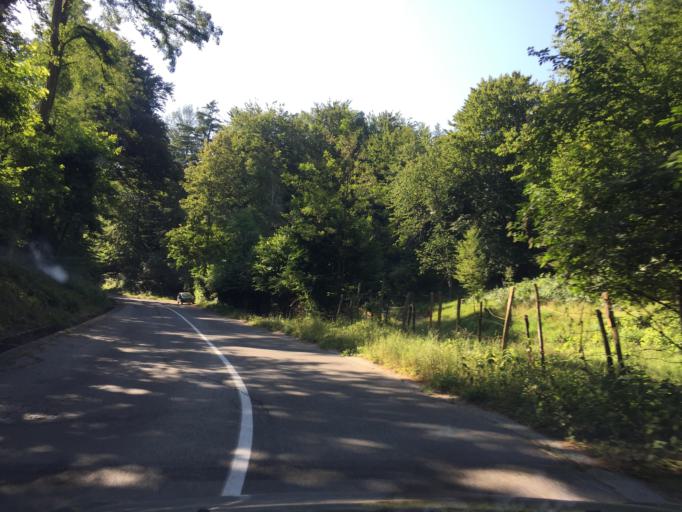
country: HR
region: Primorsko-Goranska
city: Klana
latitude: 45.4392
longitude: 14.3836
